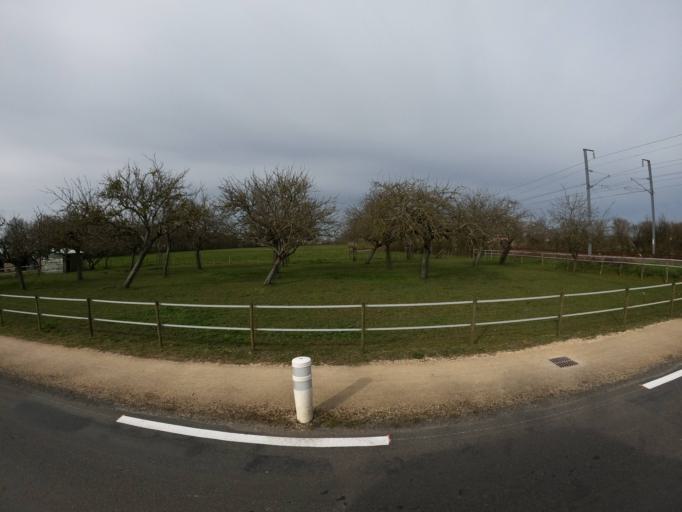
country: FR
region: Pays de la Loire
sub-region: Departement de la Vendee
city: Bouffere
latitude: 46.9570
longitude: -1.3283
